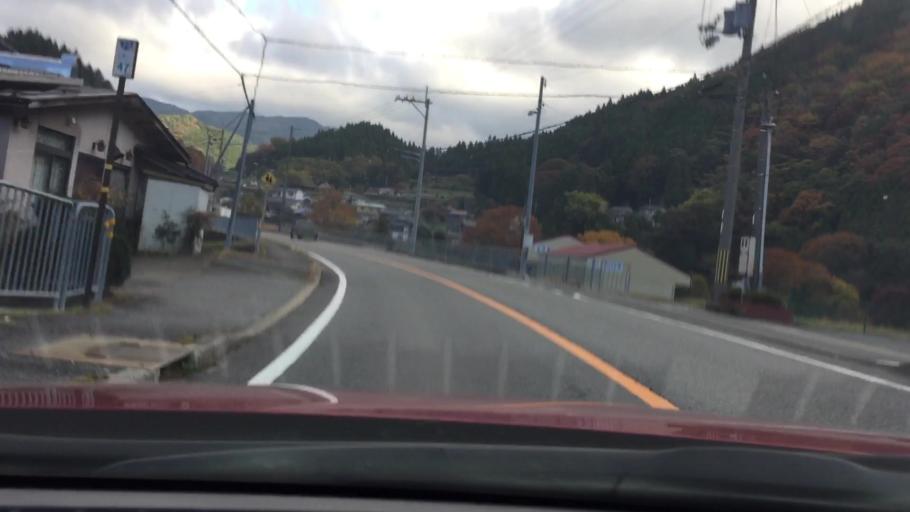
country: JP
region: Hyogo
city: Yamazakicho-nakabirose
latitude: 35.1563
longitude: 134.5456
